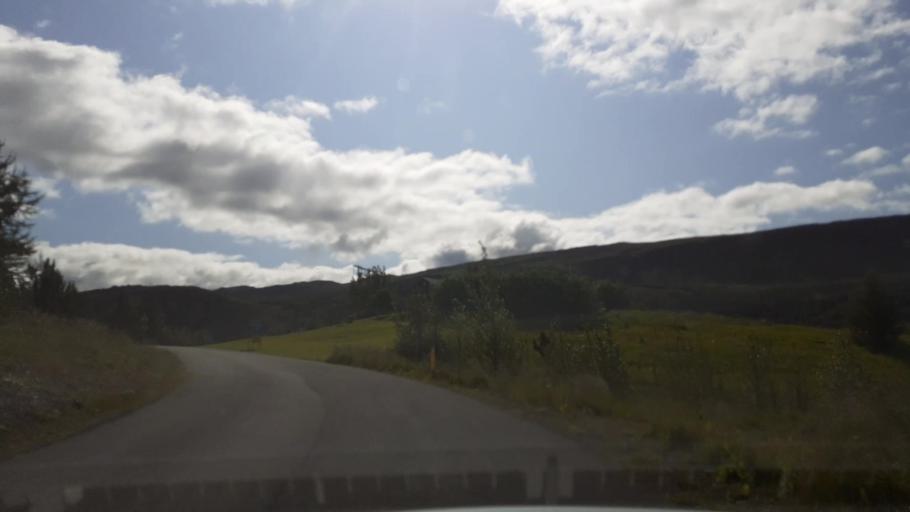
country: IS
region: Northeast
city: Akureyri
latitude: 65.6495
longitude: -18.1019
